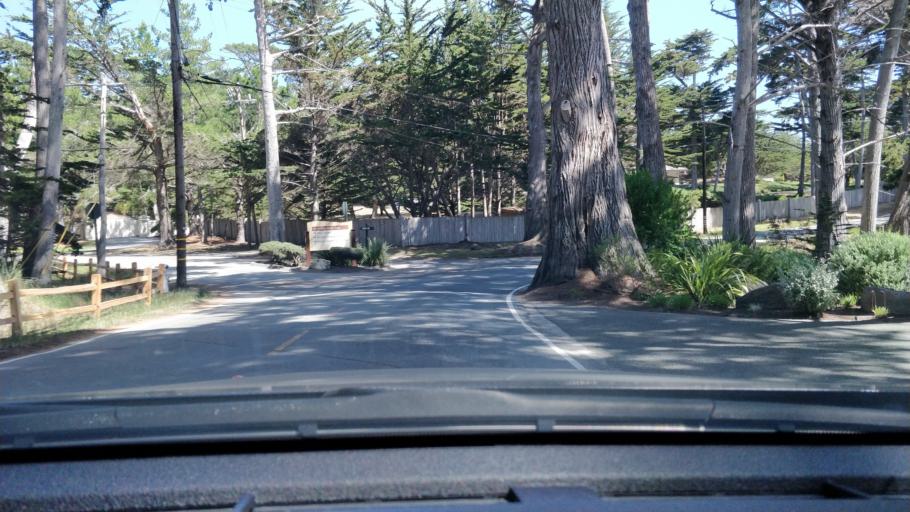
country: US
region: California
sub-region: Monterey County
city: Del Monte Forest
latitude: 36.5759
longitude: -121.9709
